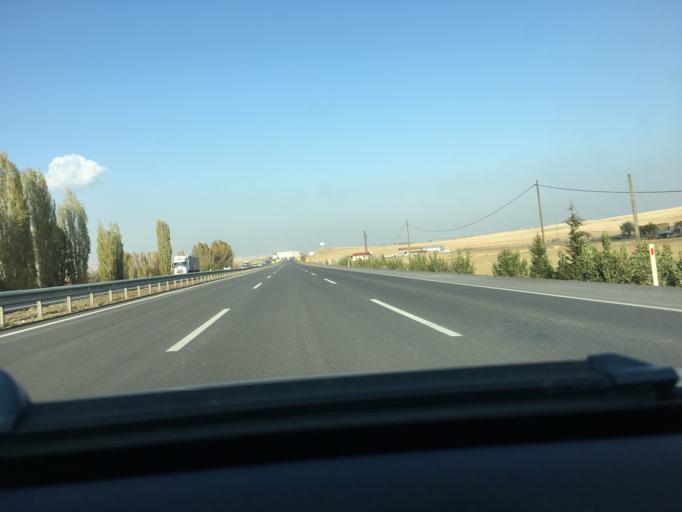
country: TR
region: Ankara
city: Polatli
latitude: 39.6736
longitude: 32.2333
